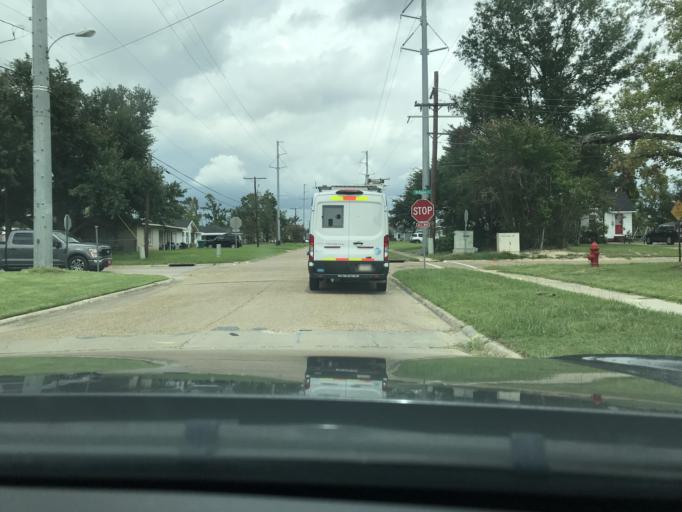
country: US
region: Louisiana
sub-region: Calcasieu Parish
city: Westlake
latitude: 30.2475
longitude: -93.2537
